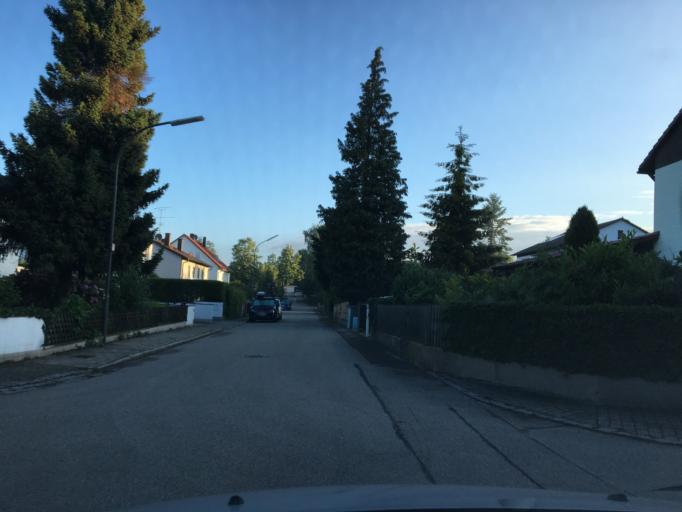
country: DE
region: Bavaria
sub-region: Upper Bavaria
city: Haimhausen
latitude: 48.3163
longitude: 11.5583
